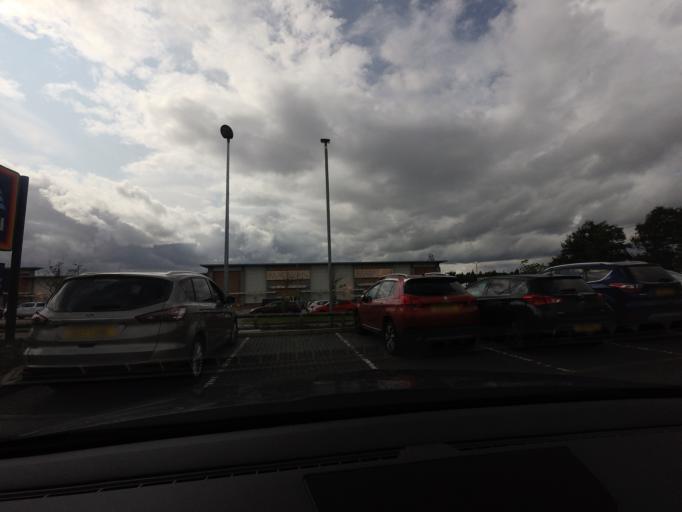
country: GB
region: Scotland
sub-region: Highland
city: Inverness
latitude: 57.4686
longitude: -4.1895
